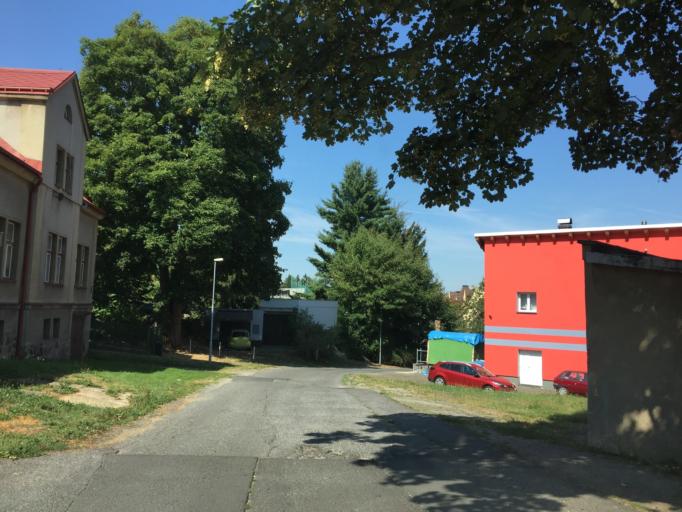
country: CZ
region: Liberecky
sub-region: Okres Jablonec nad Nisou
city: Jablonec nad Nisou
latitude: 50.7149
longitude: 15.1682
